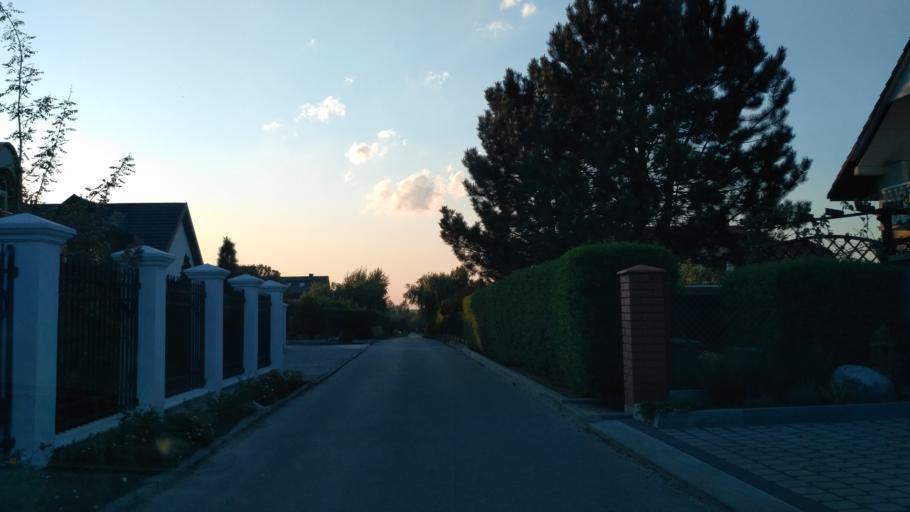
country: PL
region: Subcarpathian Voivodeship
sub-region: Powiat rzeszowski
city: Krasne
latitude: 50.0197
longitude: 22.0493
